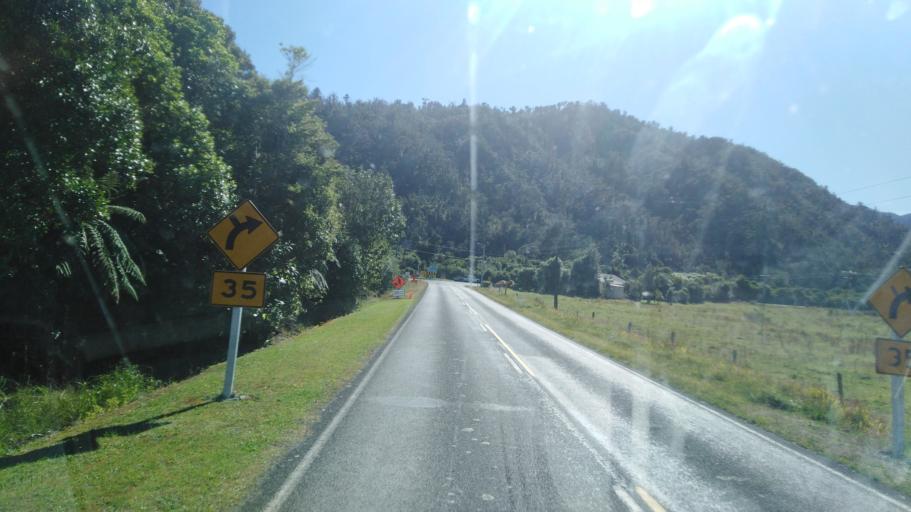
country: NZ
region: West Coast
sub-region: Buller District
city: Westport
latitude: -41.5299
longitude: 171.9429
